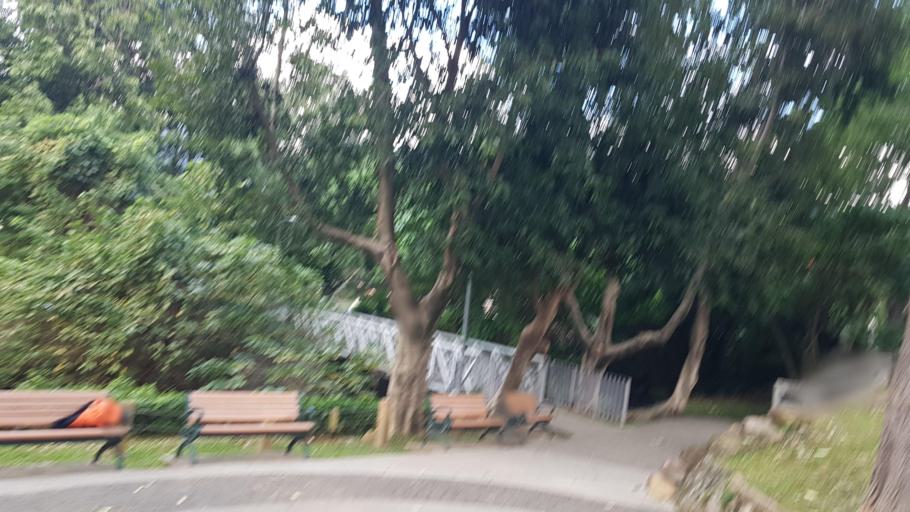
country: TW
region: Taipei
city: Taipei
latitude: 25.1397
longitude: 121.5037
